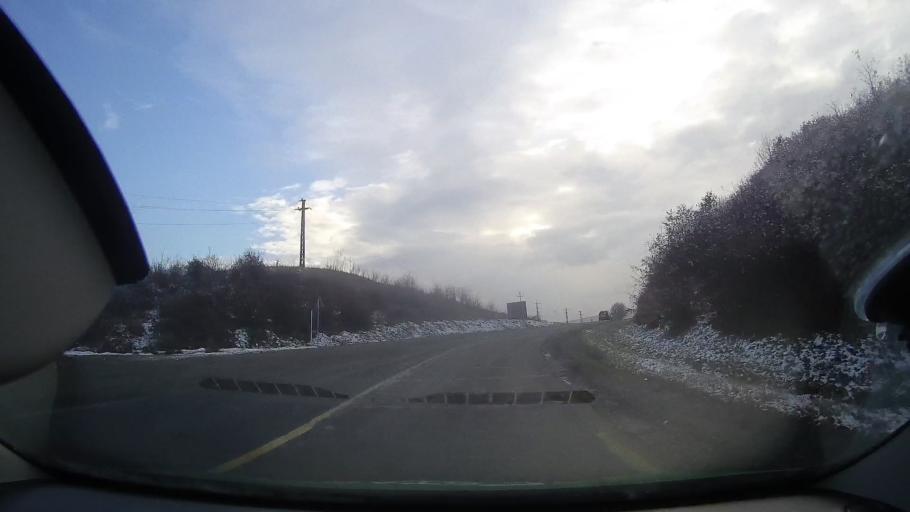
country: RO
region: Mures
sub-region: Comuna Iernut
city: Iernut
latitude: 46.4285
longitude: 24.2604
